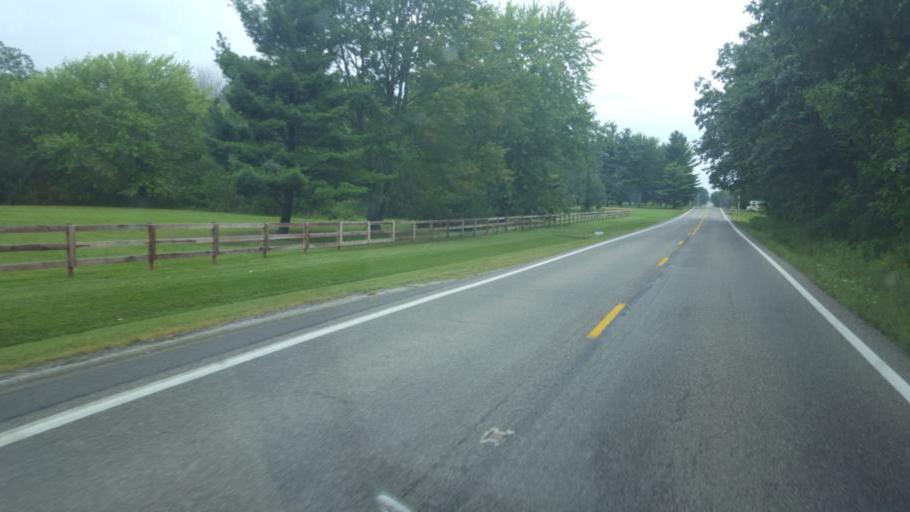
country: US
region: Ohio
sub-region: Morrow County
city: Mount Gilead
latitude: 40.6219
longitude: -82.7659
